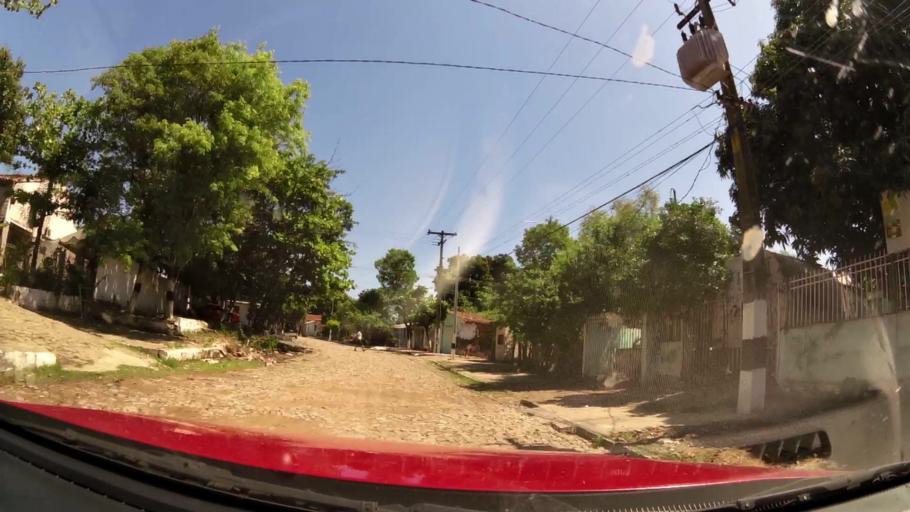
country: PY
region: Central
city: Colonia Mariano Roque Alonso
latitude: -25.2468
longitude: -57.5559
